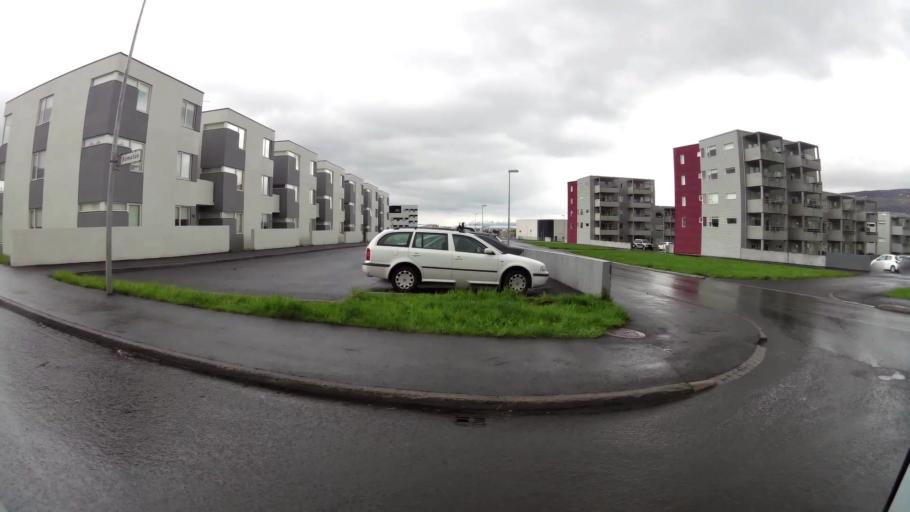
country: IS
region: Northeast
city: Akureyri
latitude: 65.6630
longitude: -18.0997
